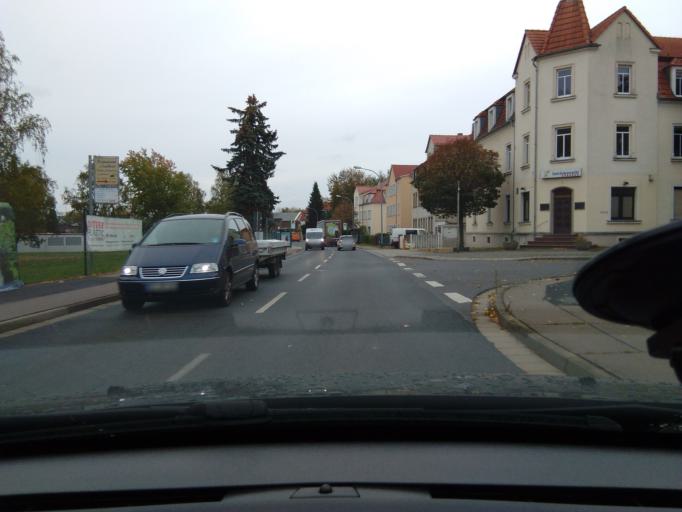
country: DE
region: Saxony
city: Niederau
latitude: 51.1477
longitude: 13.5370
